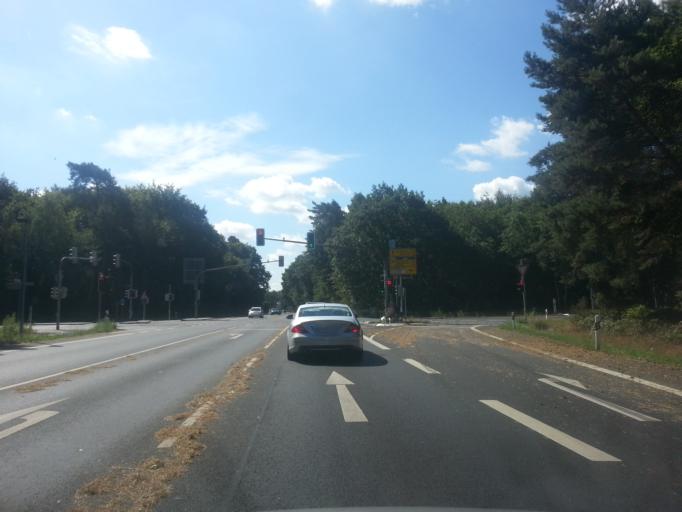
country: DE
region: Hesse
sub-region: Regierungsbezirk Darmstadt
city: Dietzenbach
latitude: 50.0084
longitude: 8.8096
